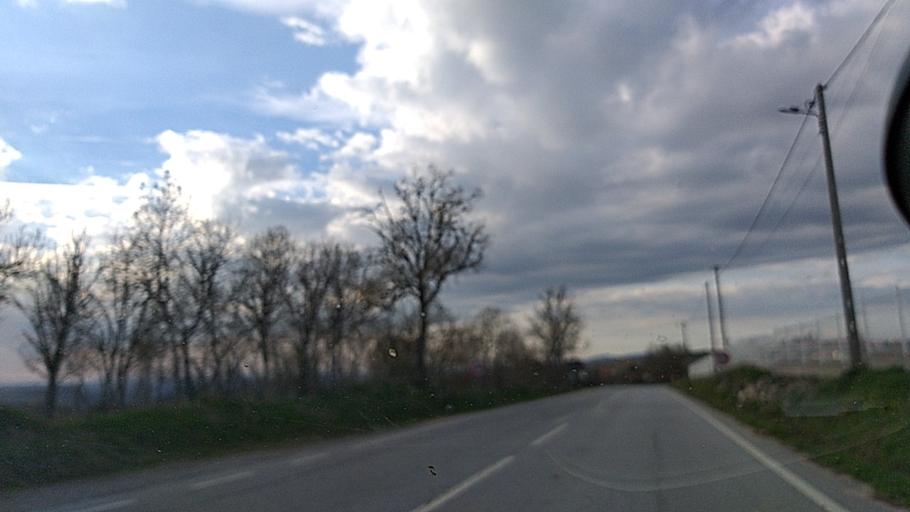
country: ES
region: Castille and Leon
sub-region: Provincia de Salamanca
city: Aldea del Obispo
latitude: 40.7137
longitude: -6.8997
